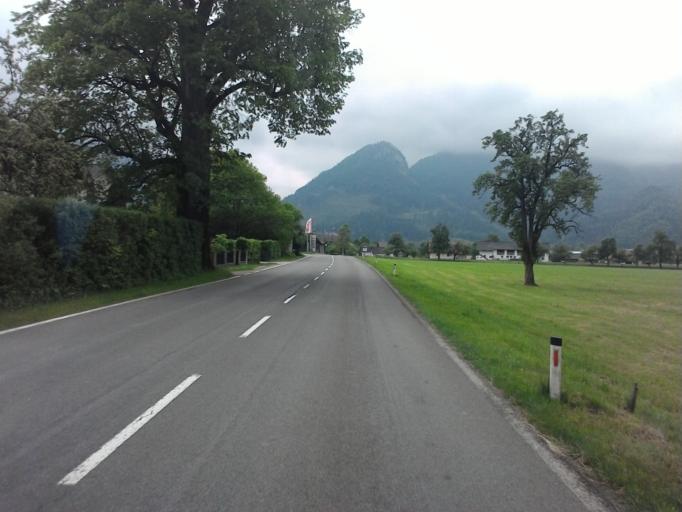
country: AT
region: Styria
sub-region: Politischer Bezirk Liezen
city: Gams bei Hieflau
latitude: 47.6552
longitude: 14.7649
